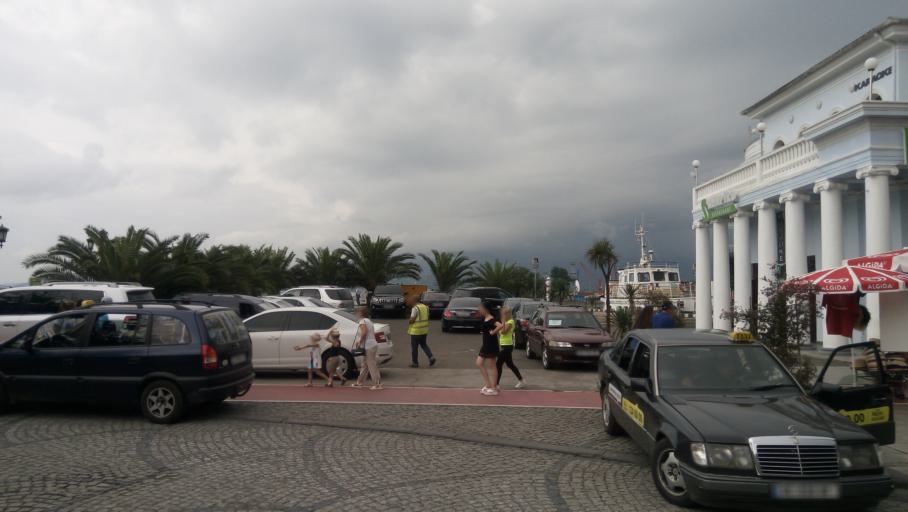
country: GE
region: Ajaria
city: Batumi
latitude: 41.6492
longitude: 41.6449
